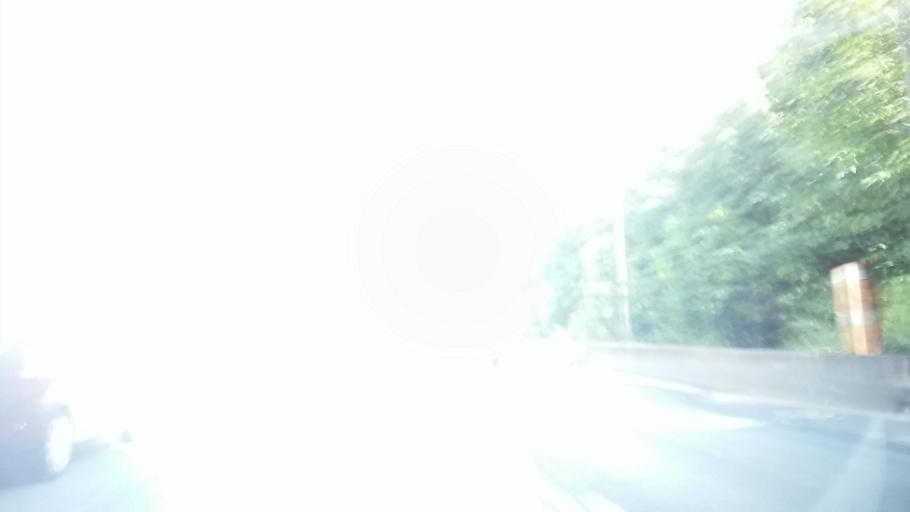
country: FR
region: Ile-de-France
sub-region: Departement du Val-de-Marne
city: Fresnes
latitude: 48.7574
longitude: 2.3287
